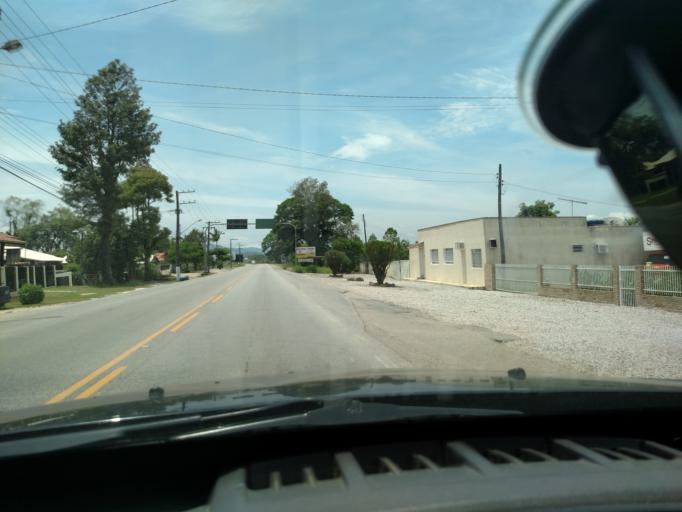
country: BR
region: Santa Catarina
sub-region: Gaspar
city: Gaspar
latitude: -26.9102
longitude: -48.9293
